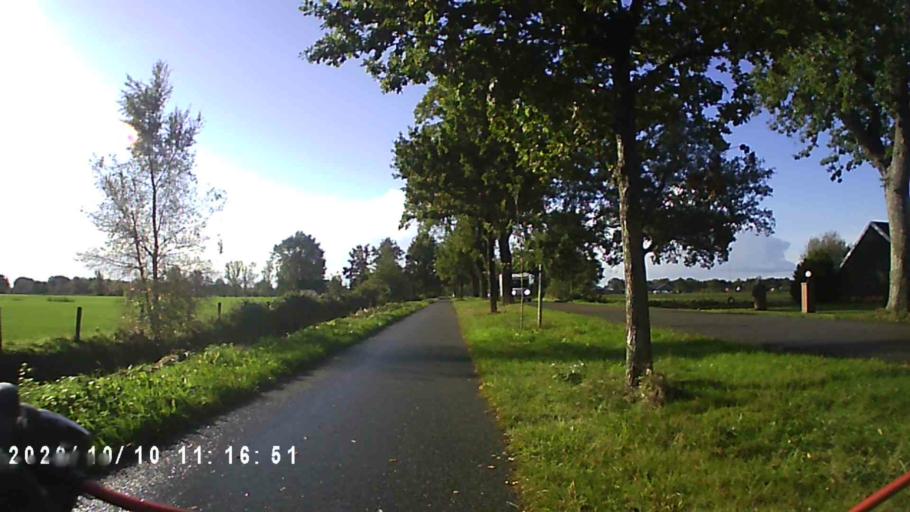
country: NL
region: Friesland
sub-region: Gemeente Smallingerland
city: Drachtstercompagnie
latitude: 53.0983
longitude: 6.1991
